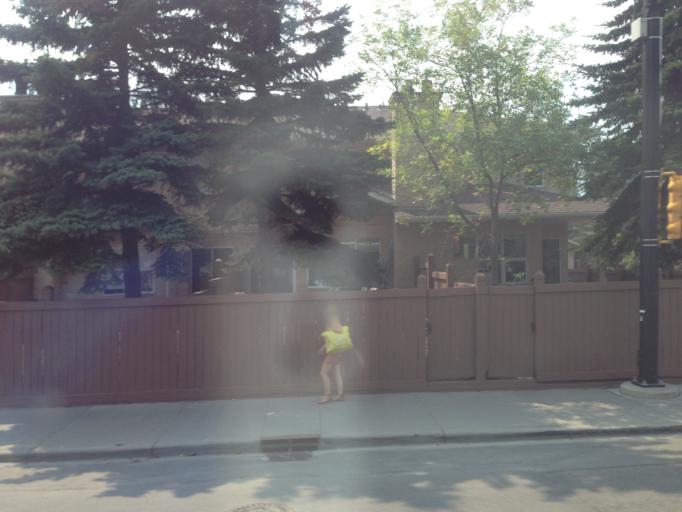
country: CA
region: Alberta
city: Canmore
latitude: 51.0920
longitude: -115.3573
